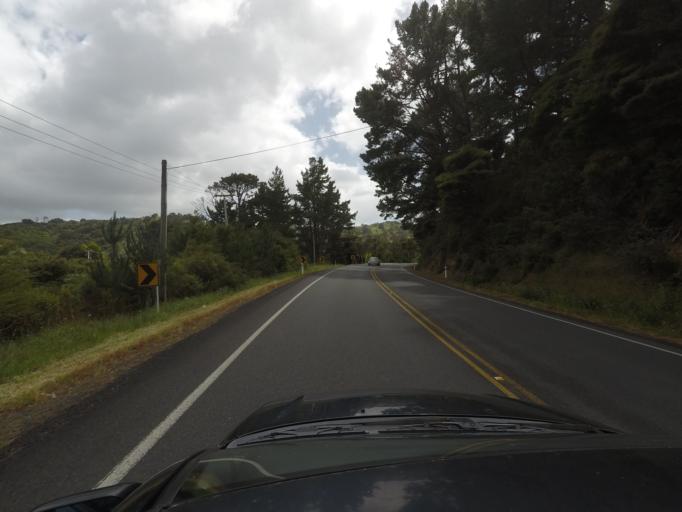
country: NZ
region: Auckland
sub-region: Auckland
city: Warkworth
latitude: -36.5593
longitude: 174.6971
